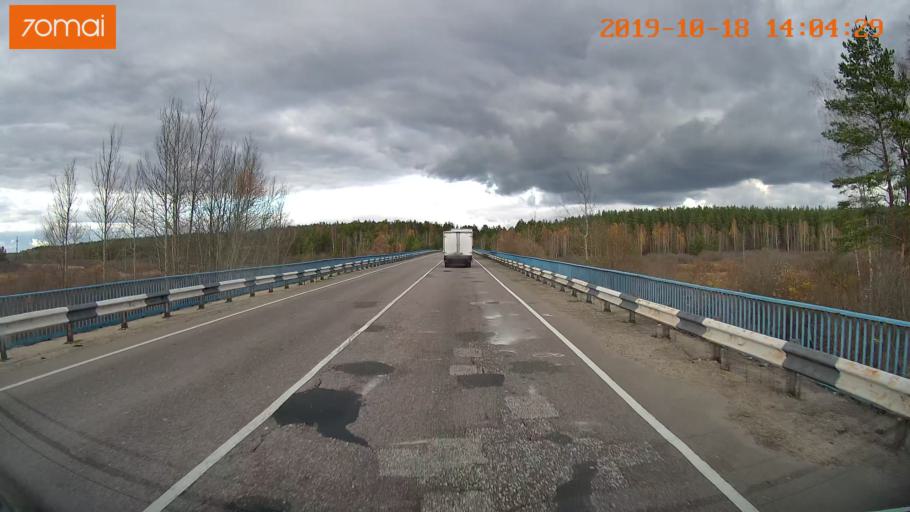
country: RU
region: Rjazan
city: Spas-Klepiki
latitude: 55.1264
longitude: 40.1335
